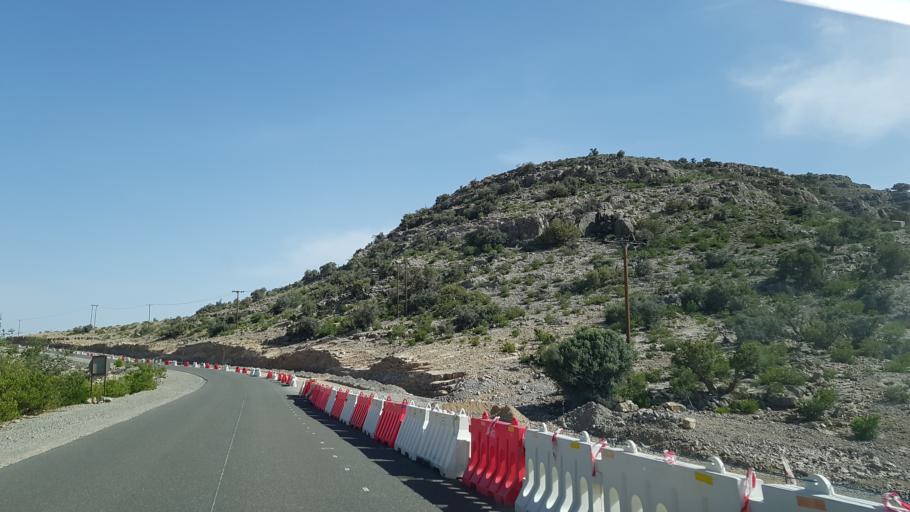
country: OM
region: Muhafazat ad Dakhiliyah
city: Izki
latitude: 23.1079
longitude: 57.6607
